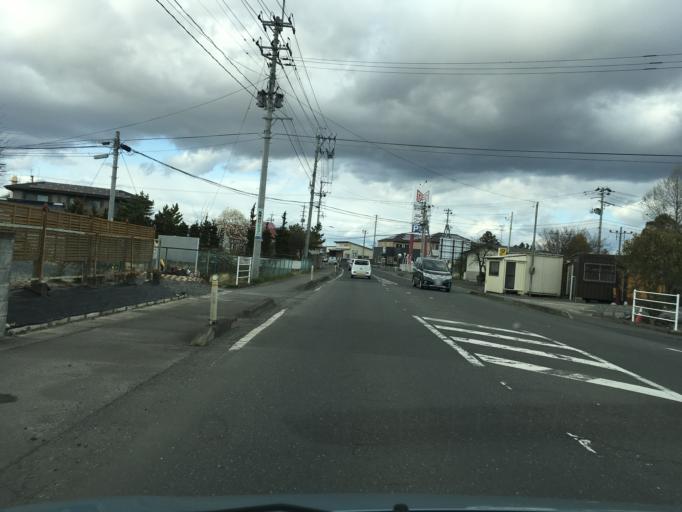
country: JP
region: Miyagi
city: Wakuya
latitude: 38.6740
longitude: 141.1919
